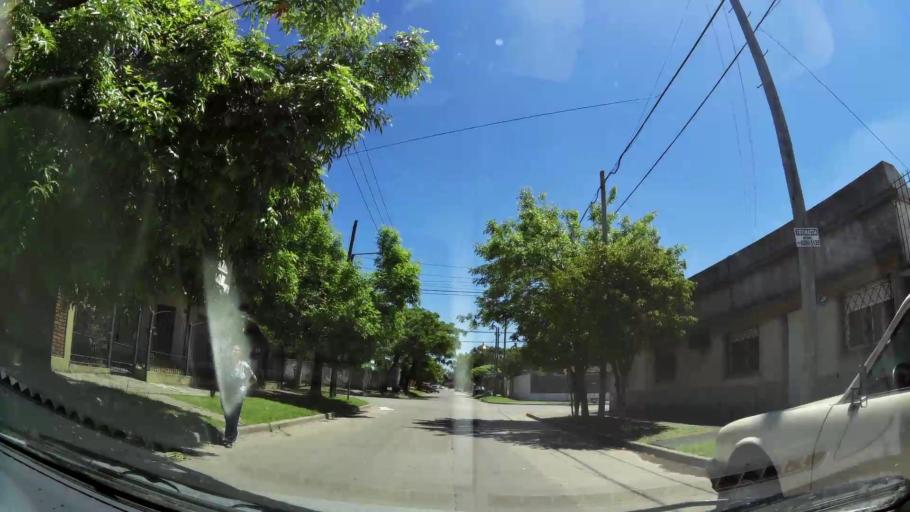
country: AR
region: Buenos Aires
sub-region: Partido de Quilmes
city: Quilmes
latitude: -34.7200
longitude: -58.3125
